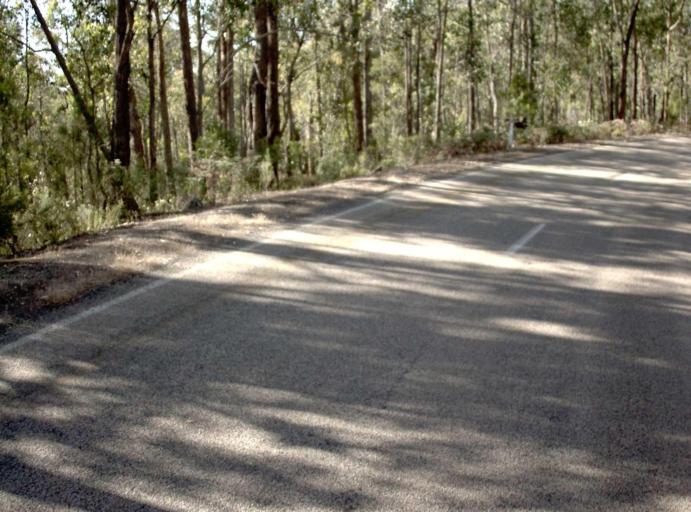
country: AU
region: Victoria
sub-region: East Gippsland
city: Lakes Entrance
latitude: -37.5643
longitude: 148.5590
